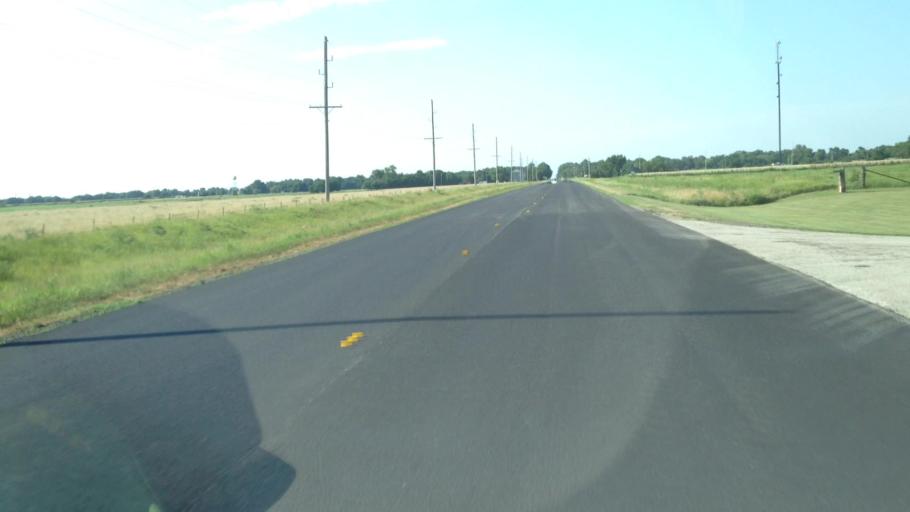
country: US
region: Kansas
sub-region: Allen County
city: Iola
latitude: 37.9009
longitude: -95.1704
